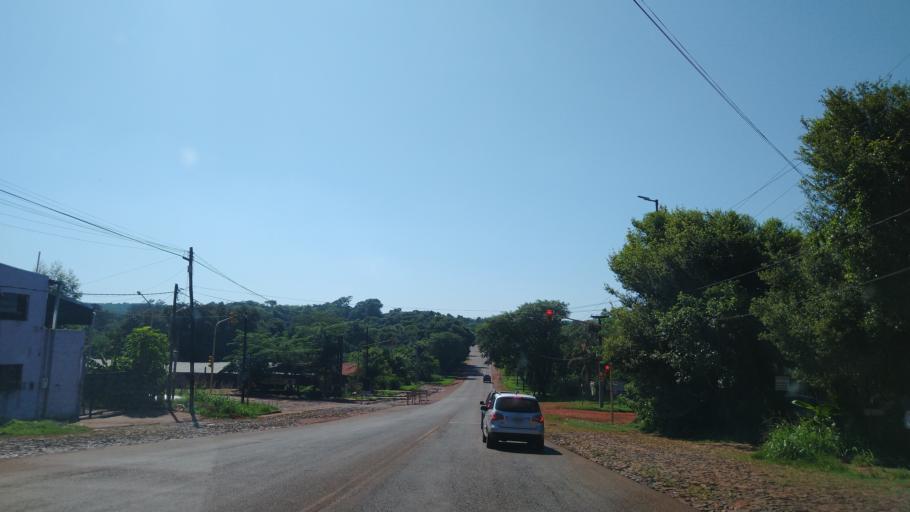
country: AR
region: Misiones
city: Puerto Esperanza
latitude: -26.0223
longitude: -54.6034
